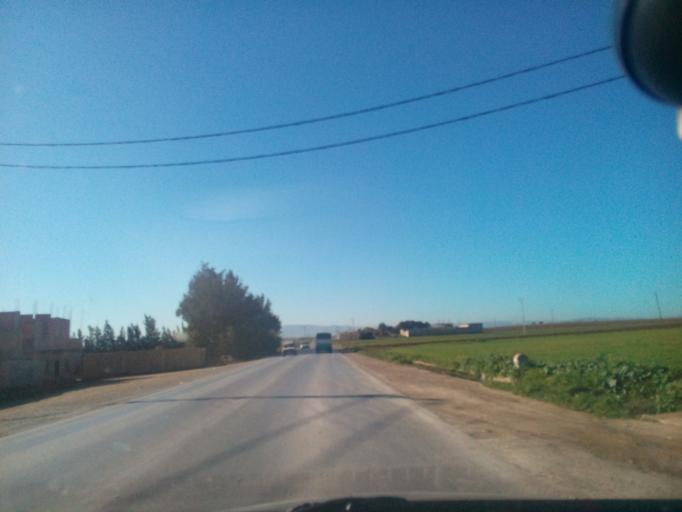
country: DZ
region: Relizane
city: Djidiouia
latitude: 35.8947
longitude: 0.6650
